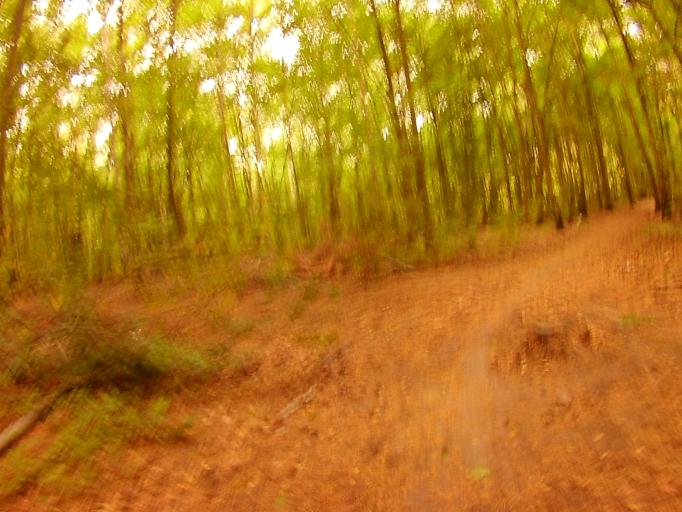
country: DE
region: Berlin
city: Grunau
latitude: 52.4071
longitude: 13.5943
